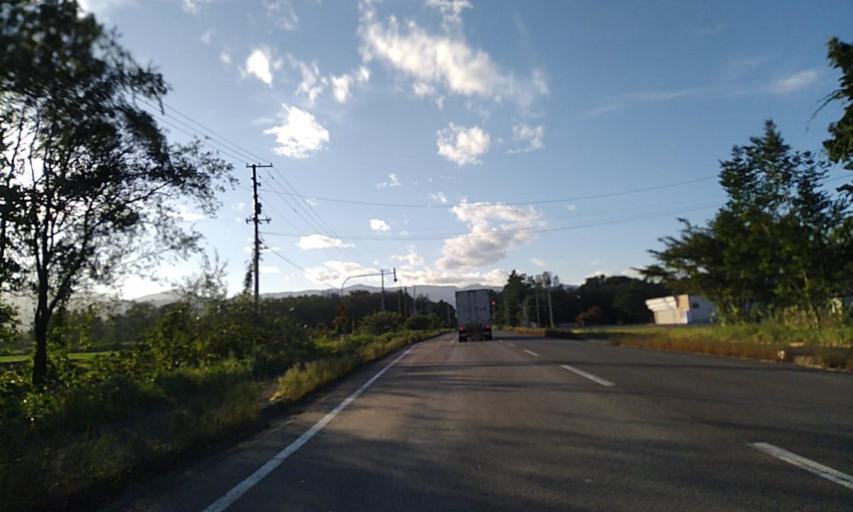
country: JP
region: Hokkaido
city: Otofuke
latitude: 42.9586
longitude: 142.9095
